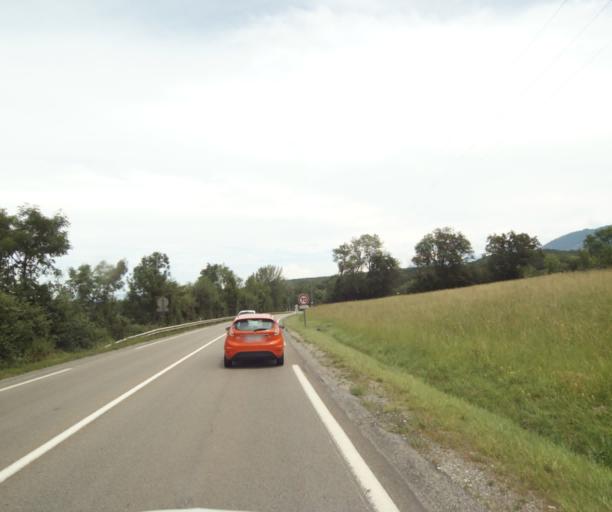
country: FR
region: Rhone-Alpes
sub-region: Departement de la Haute-Savoie
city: Allinges
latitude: 46.3400
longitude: 6.4592
